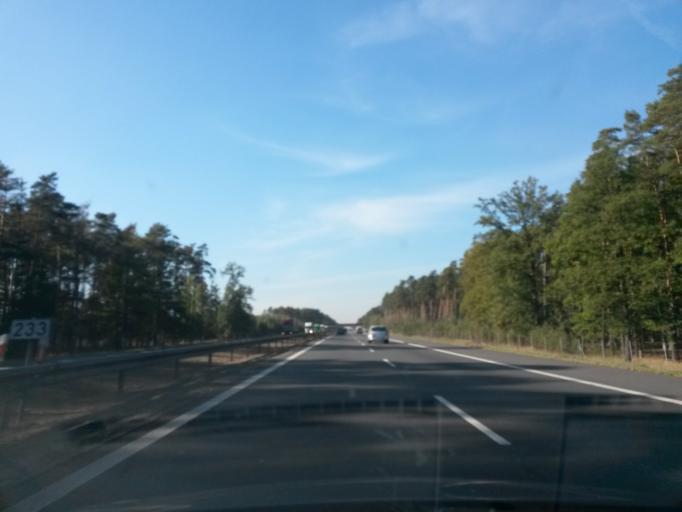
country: PL
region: Opole Voivodeship
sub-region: Powiat opolski
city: Komprachcice
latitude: 50.5965
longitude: 17.7995
